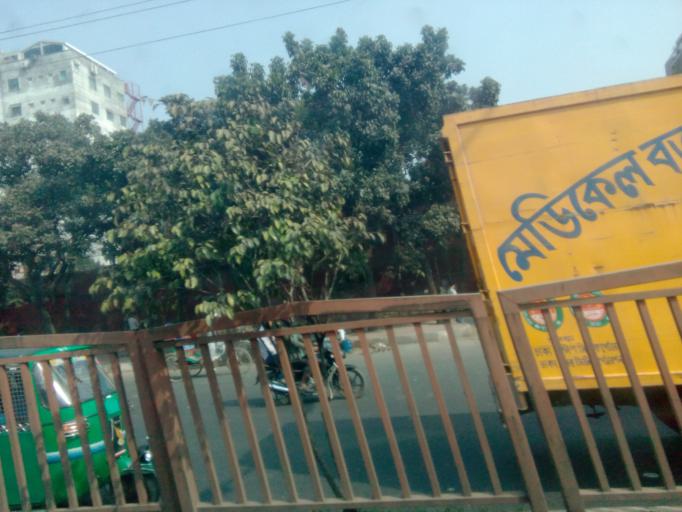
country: BD
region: Dhaka
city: Paltan
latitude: 23.7944
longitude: 90.4244
